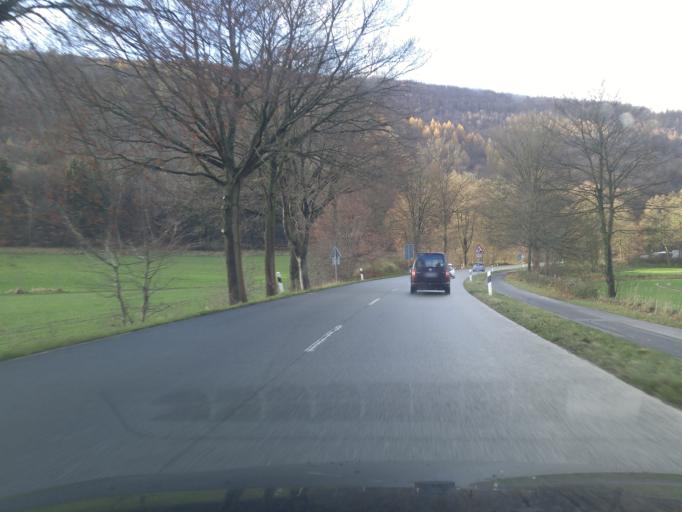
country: DE
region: Lower Saxony
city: Hannoversch Munden
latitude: 51.4508
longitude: 9.6326
